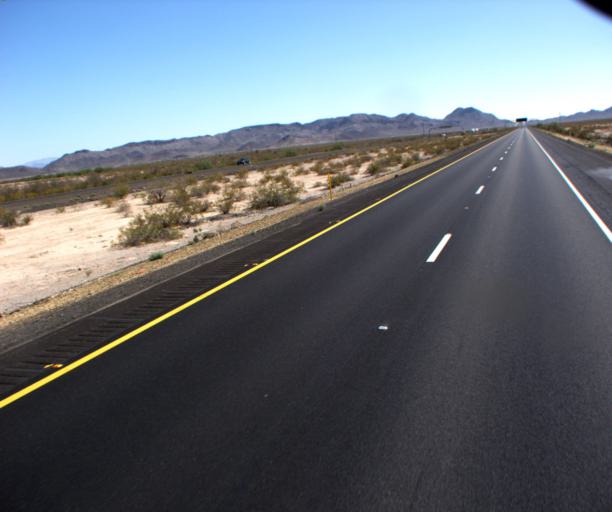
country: US
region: Arizona
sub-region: La Paz County
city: Salome
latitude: 33.6213
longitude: -113.7040
